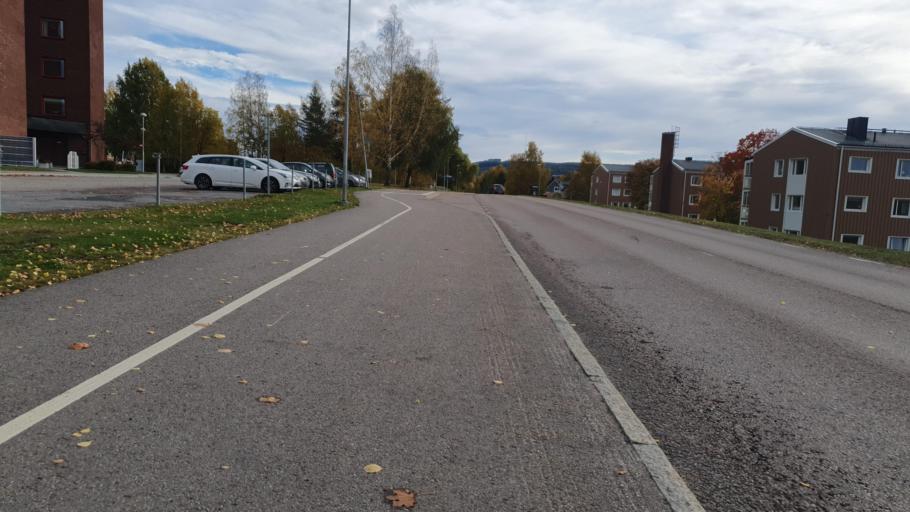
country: SE
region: Vaesternorrland
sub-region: Sundsvalls Kommun
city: Sundsvall
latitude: 62.4033
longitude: 17.2516
